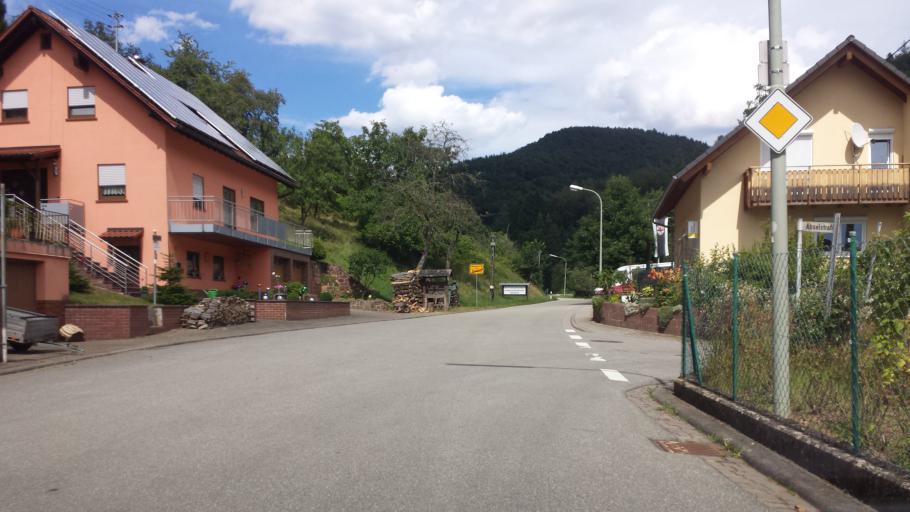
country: DE
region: Rheinland-Pfalz
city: Ramberg
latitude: 49.2654
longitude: 8.0114
